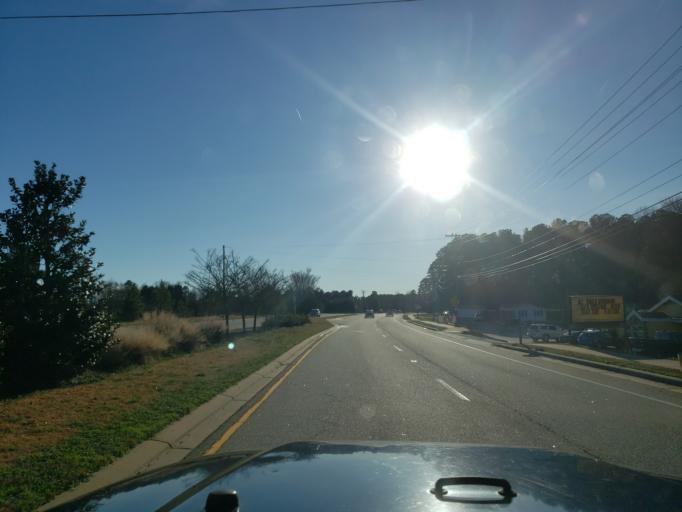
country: US
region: North Carolina
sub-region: Catawba County
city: Lake Norman of Catawba
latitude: 35.5578
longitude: -80.9211
